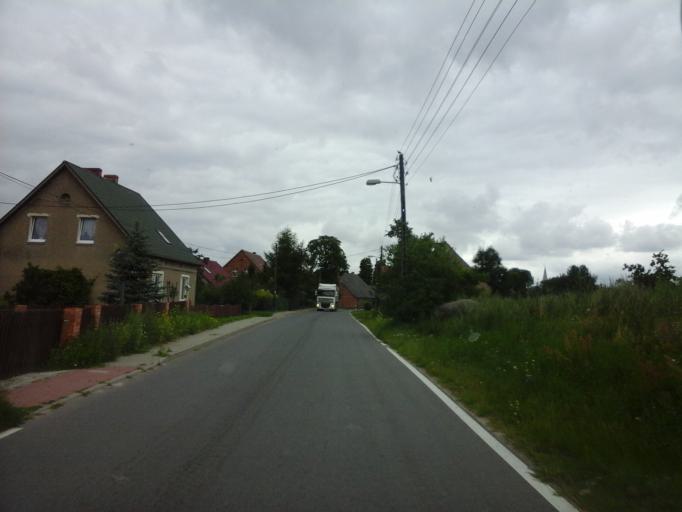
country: PL
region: West Pomeranian Voivodeship
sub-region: Powiat choszczenski
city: Krzecin
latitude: 52.9996
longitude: 15.4245
